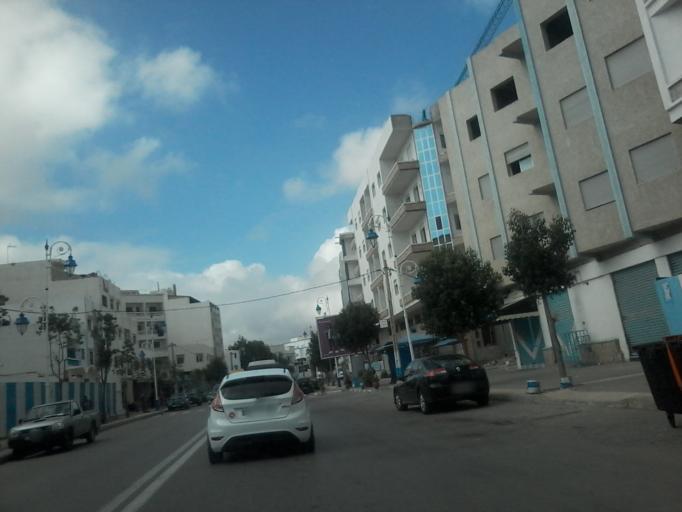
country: MA
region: Tanger-Tetouan
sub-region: Tetouan
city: Martil
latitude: 35.6268
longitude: -5.2798
